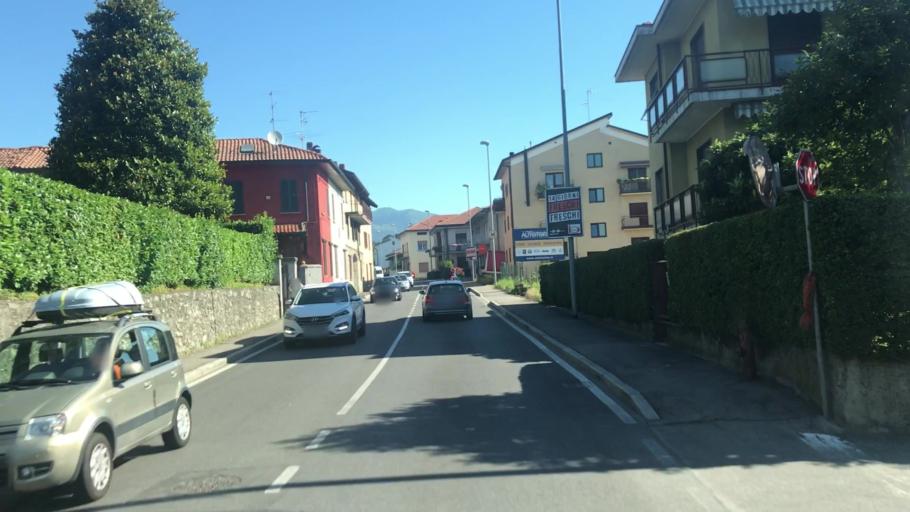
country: IT
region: Lombardy
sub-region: Provincia di Como
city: Senna Comasco
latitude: 45.7508
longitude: 9.1239
